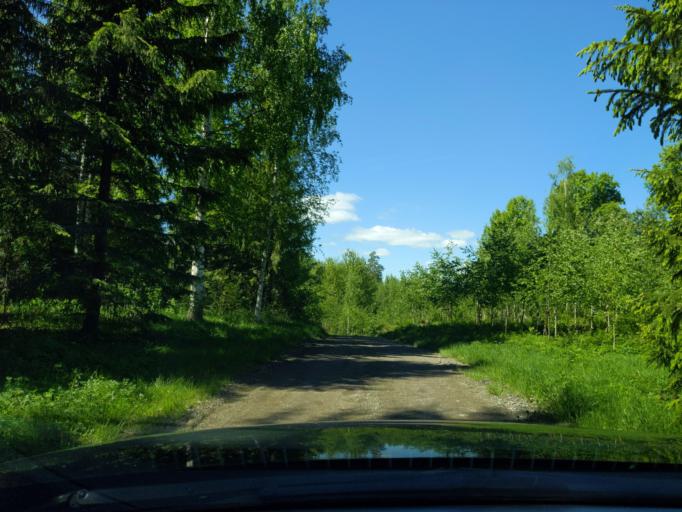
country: FI
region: Paijanne Tavastia
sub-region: Lahti
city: Lahti
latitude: 61.0542
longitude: 25.6912
